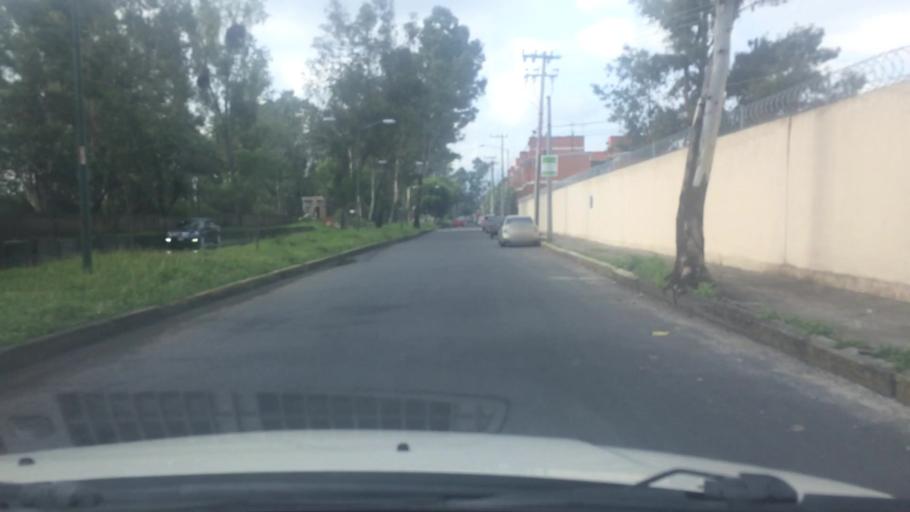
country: MX
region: Mexico City
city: Xochimilco
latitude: 19.3107
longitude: -99.1001
